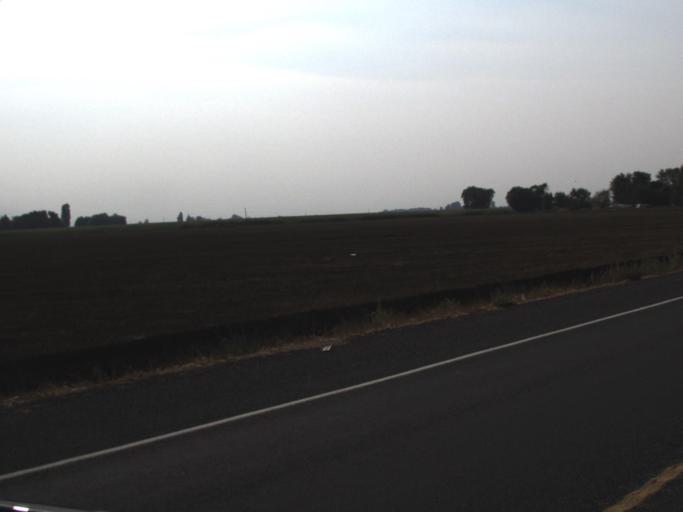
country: US
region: Washington
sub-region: Yakima County
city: Toppenish
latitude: 46.3484
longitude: -120.2771
